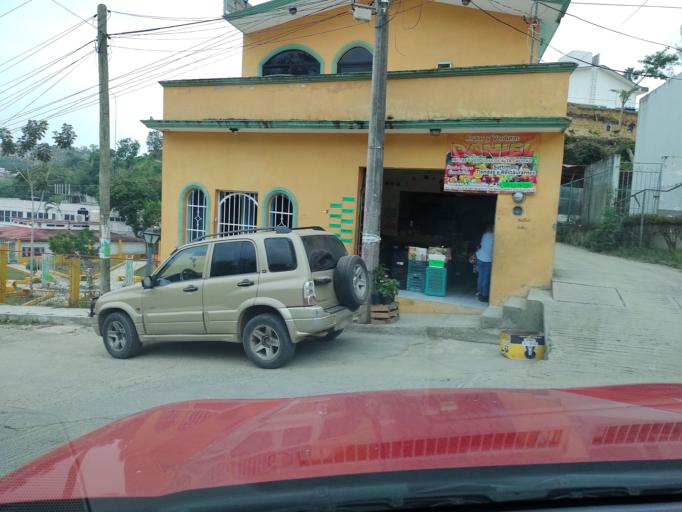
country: MX
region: Veracruz
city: Papantla de Olarte
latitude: 20.4577
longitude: -97.3306
